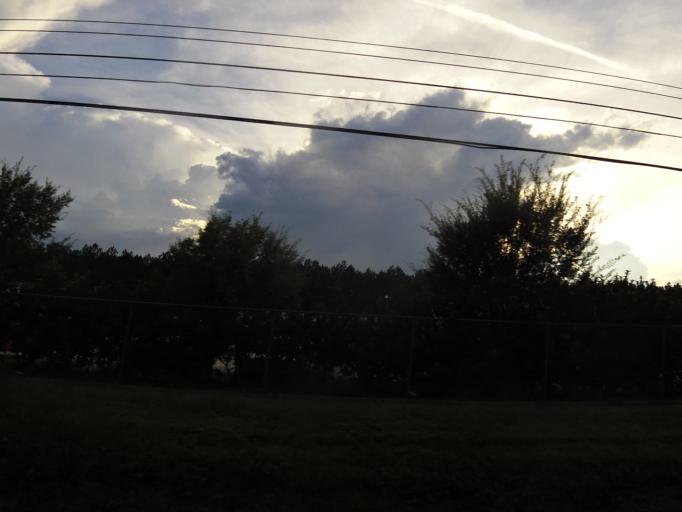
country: US
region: Florida
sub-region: Duval County
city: Jacksonville
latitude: 30.3593
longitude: -81.7731
